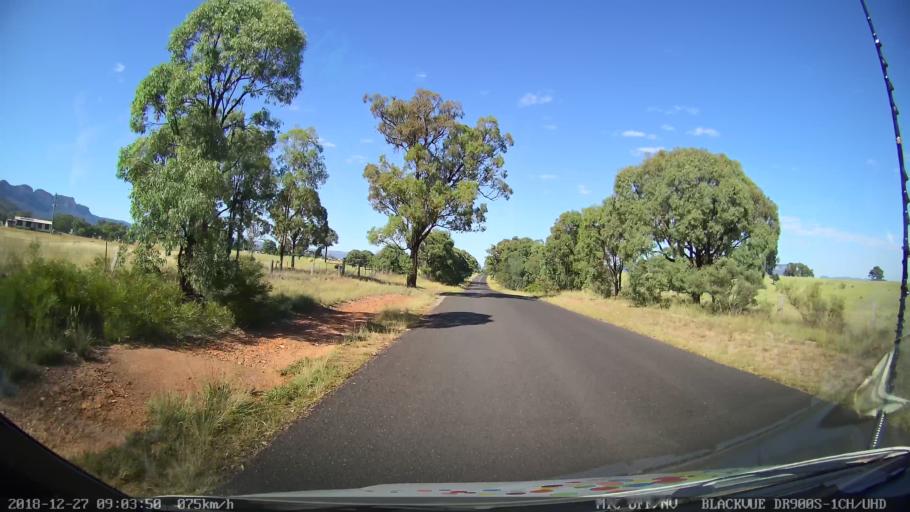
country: AU
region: New South Wales
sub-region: Lithgow
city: Portland
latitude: -33.1071
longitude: 150.1971
